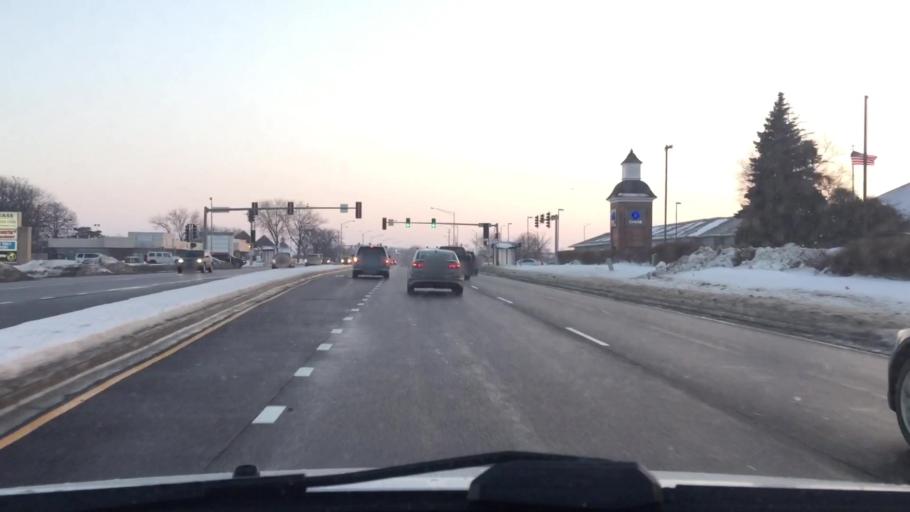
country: US
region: Illinois
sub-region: Kane County
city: Saint Charles
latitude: 41.9048
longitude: -88.3399
